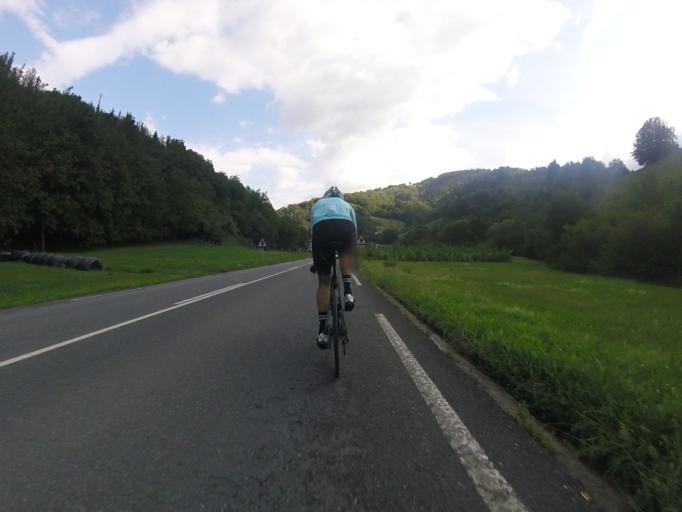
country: ES
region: Basque Country
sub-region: Provincia de Guipuzcoa
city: Amezqueta
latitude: 43.0661
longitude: -2.0857
